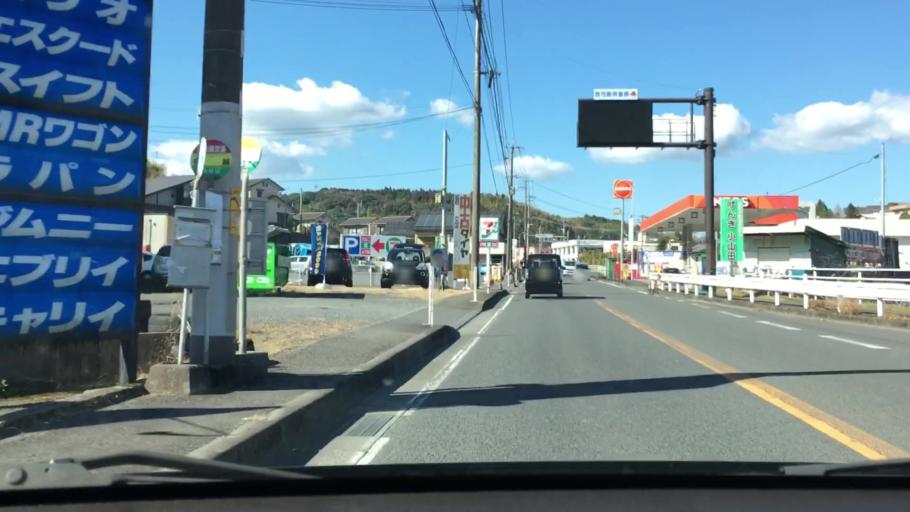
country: JP
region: Kagoshima
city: Ijuin
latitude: 31.6612
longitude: 130.4912
